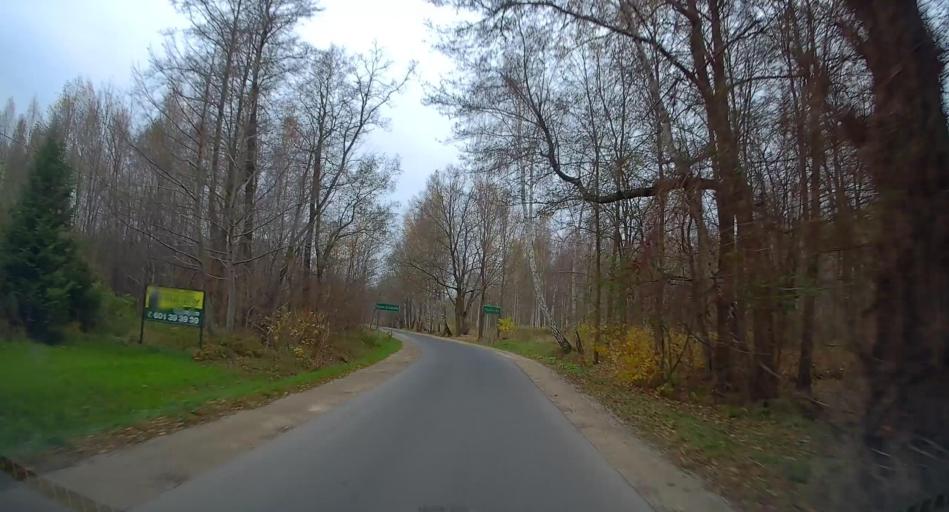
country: PL
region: Lodz Voivodeship
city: Zabia Wola
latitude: 52.0171
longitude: 20.6558
